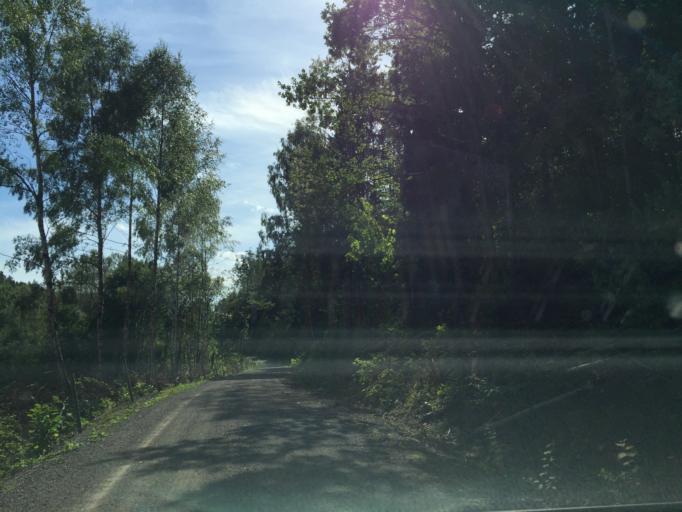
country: NO
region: Vestfold
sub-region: Hof
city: Hof
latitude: 59.4527
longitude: 10.1509
